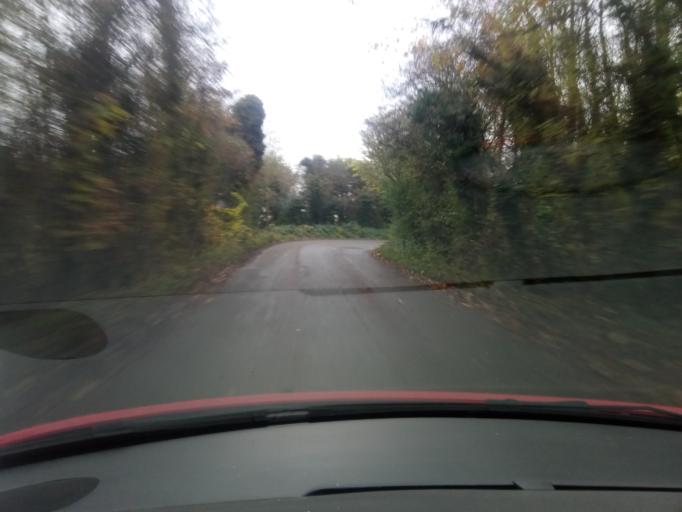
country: GB
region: England
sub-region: Derbyshire
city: Melbourne
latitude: 52.8681
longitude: -1.4261
